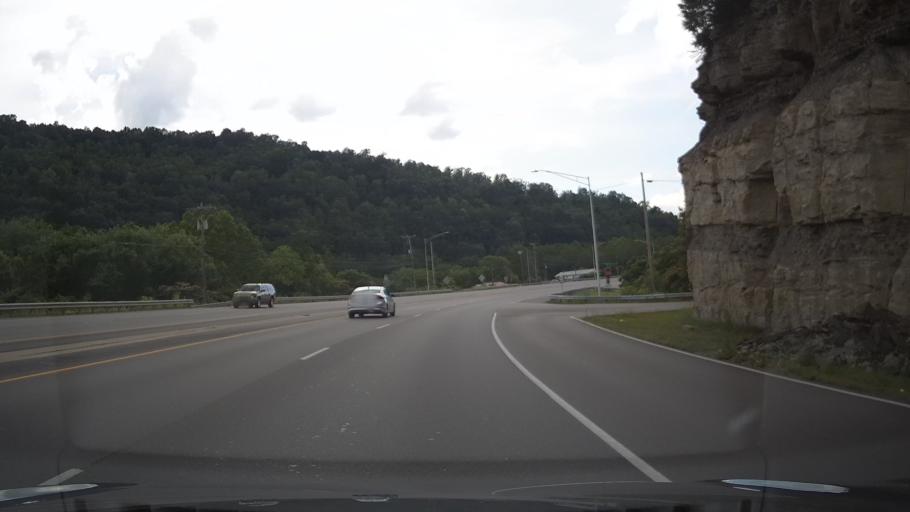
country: US
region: Kentucky
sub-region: Floyd County
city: Prestonsburg
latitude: 37.6034
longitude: -82.6978
